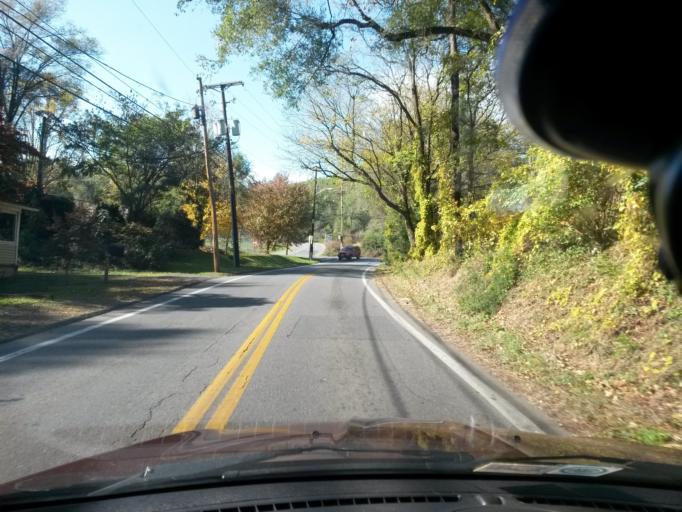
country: US
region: Virginia
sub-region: City of Roanoke
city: Roanoke
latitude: 37.2935
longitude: -79.9247
